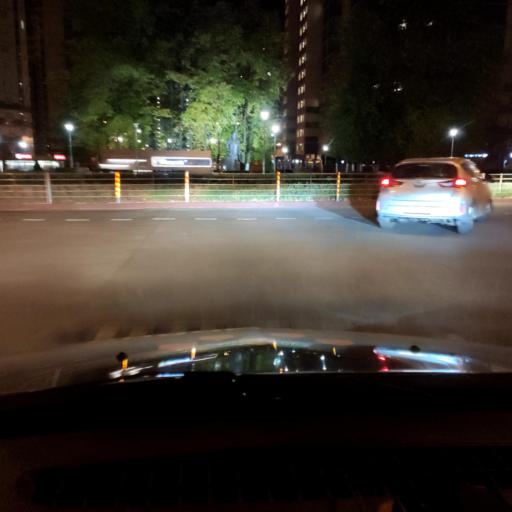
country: RU
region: Voronezj
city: Voronezh
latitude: 51.7150
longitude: 39.1954
